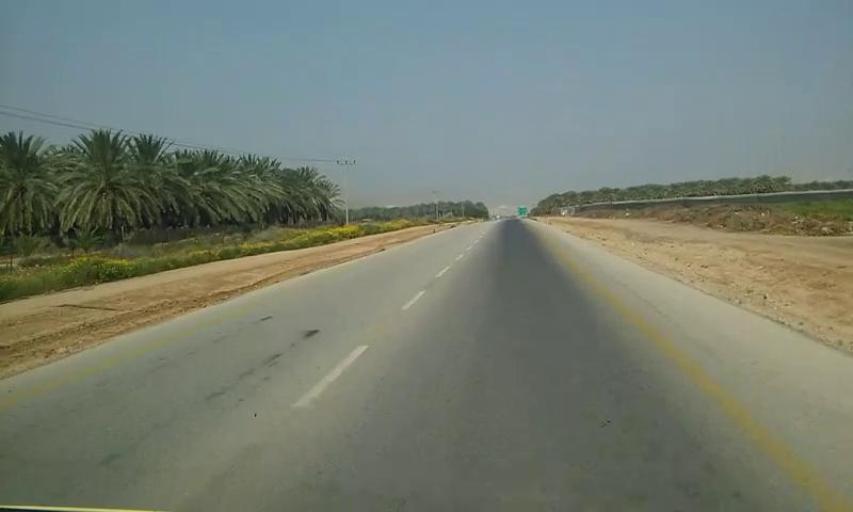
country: PS
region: West Bank
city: Al Fasayil
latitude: 31.9951
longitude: 35.4569
